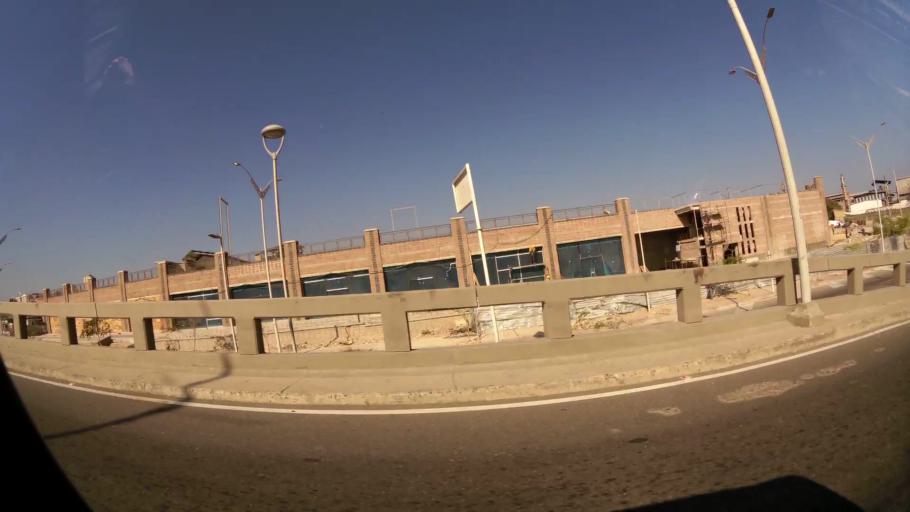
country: CO
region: Atlantico
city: Barranquilla
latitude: 10.9957
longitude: -74.7831
